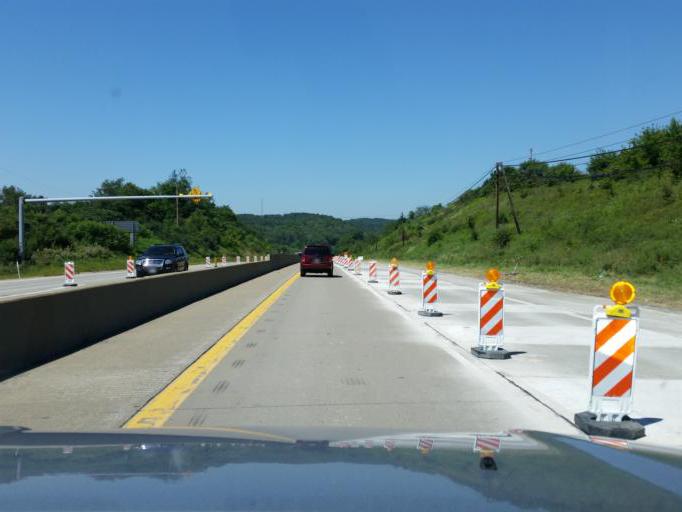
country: US
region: Pennsylvania
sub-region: Westmoreland County
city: Delmont
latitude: 40.3978
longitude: -79.4697
